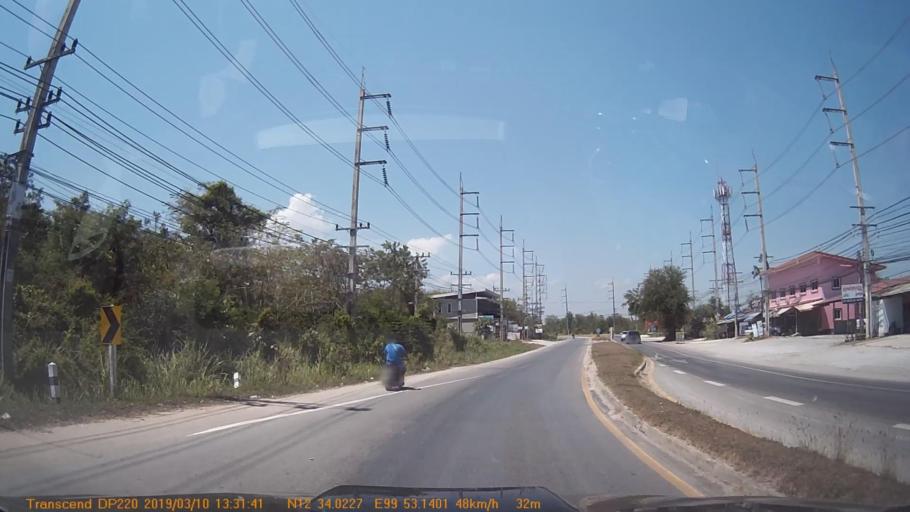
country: TH
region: Prachuap Khiri Khan
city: Hua Hin
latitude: 12.5667
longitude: 99.8857
